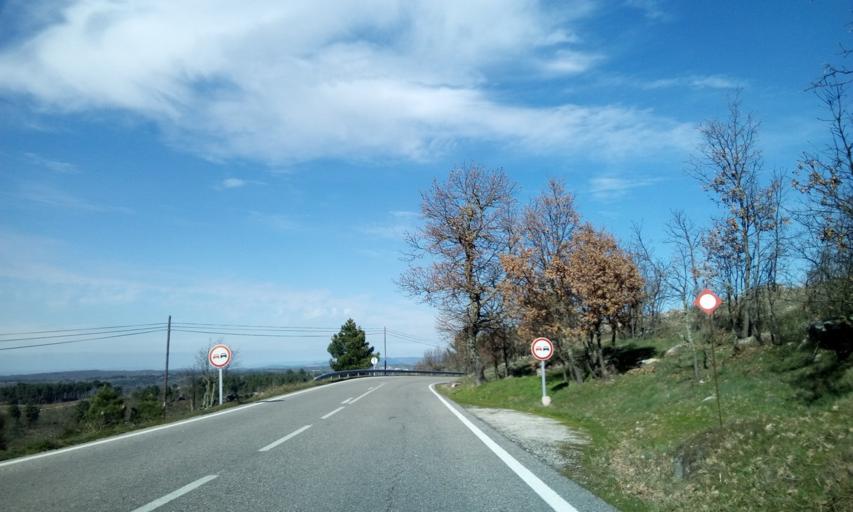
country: PT
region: Guarda
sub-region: Guarda
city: Sequeira
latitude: 40.5951
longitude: -7.1332
